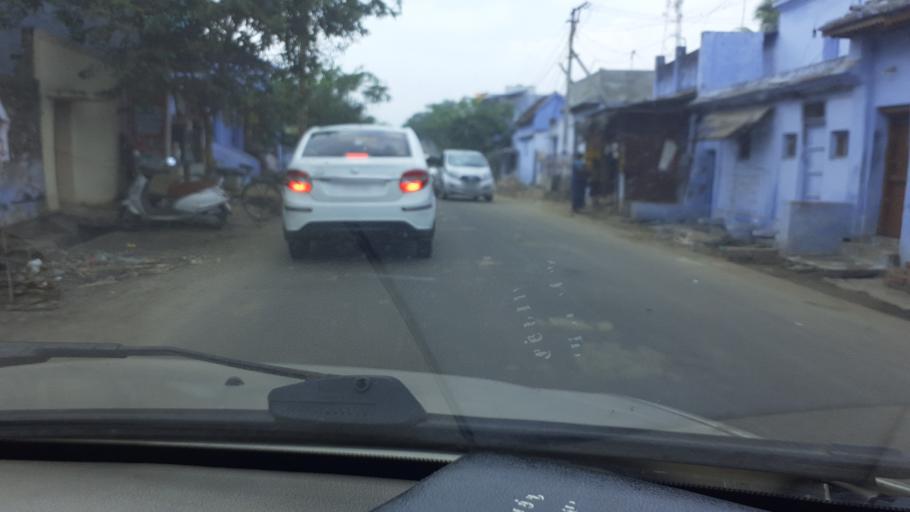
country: IN
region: Tamil Nadu
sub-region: Tirunelveli Kattabo
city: Viravanallur
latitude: 8.7216
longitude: 77.5452
